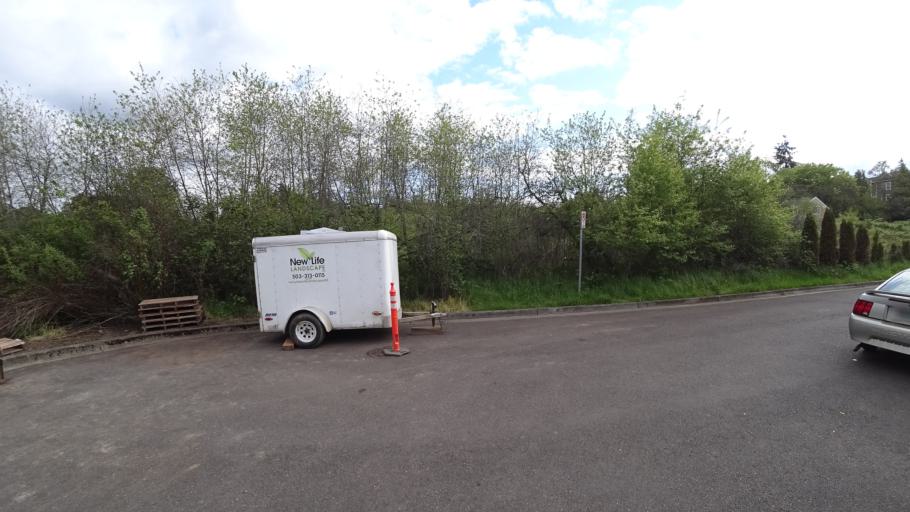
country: US
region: Oregon
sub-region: Washington County
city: Beaverton
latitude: 45.4558
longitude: -122.8351
